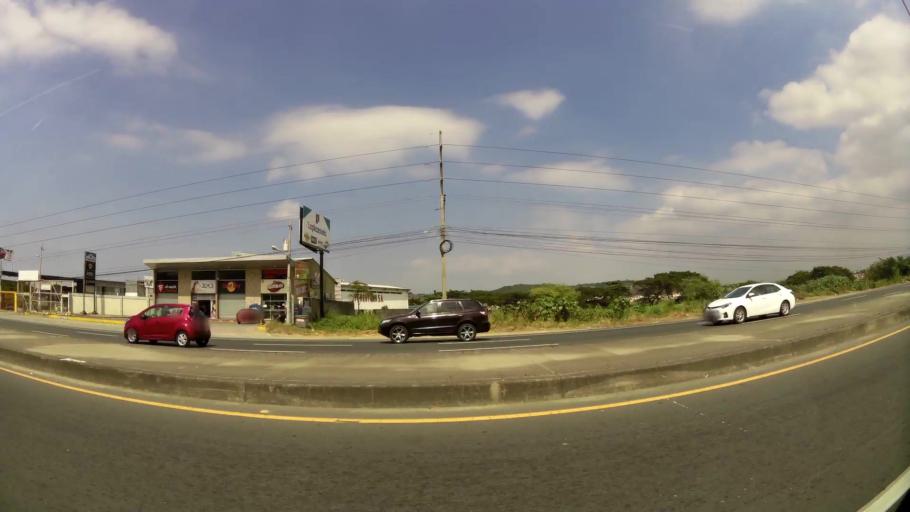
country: EC
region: Guayas
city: El Triunfo
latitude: -2.0564
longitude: -79.9197
